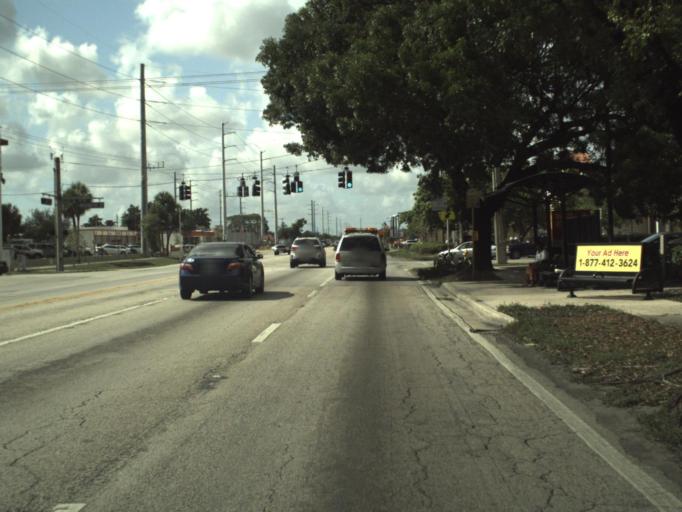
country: US
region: Florida
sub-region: Broward County
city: Pembroke Pines
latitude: 26.0032
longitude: -80.2075
